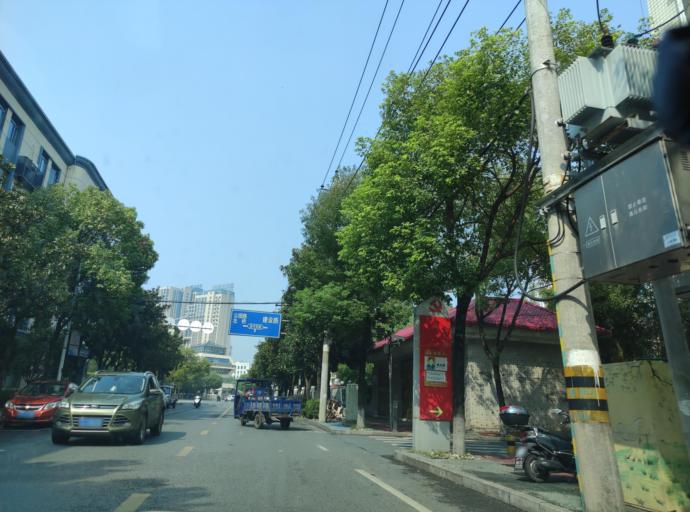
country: CN
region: Jiangxi Sheng
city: Pingxiang
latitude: 27.6439
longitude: 113.8558
